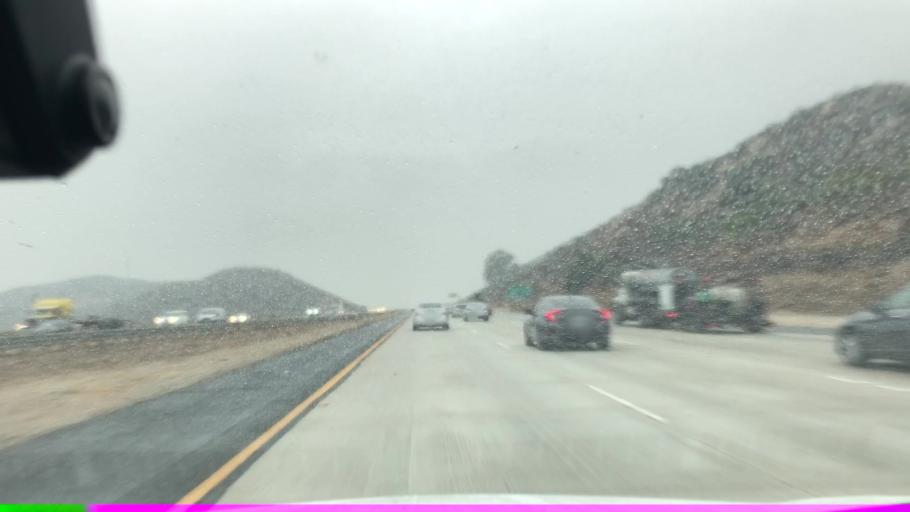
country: US
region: California
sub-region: San Diego County
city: Hidden Meadows
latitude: 33.1741
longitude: -117.1125
